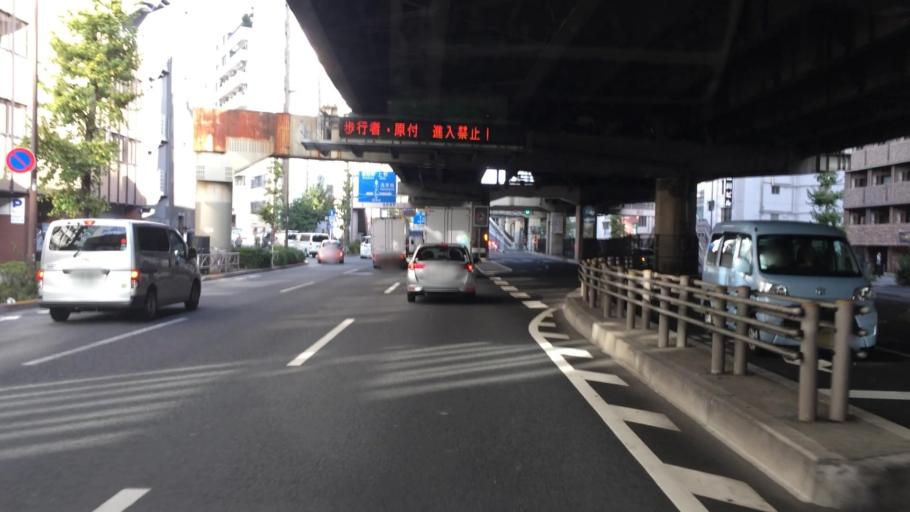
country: JP
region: Tokyo
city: Tokyo
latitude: 35.6918
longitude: 139.7747
